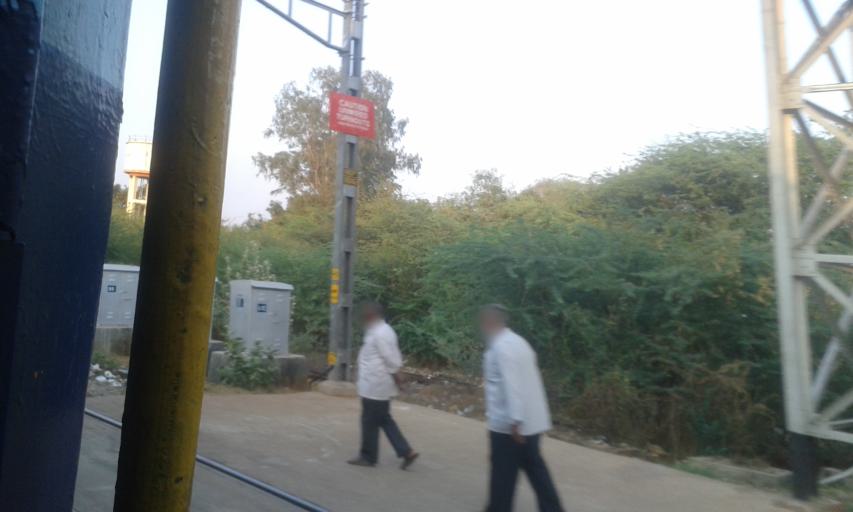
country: IN
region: Andhra Pradesh
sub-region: Anantapur
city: Hindupur
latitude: 13.8208
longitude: 77.5008
